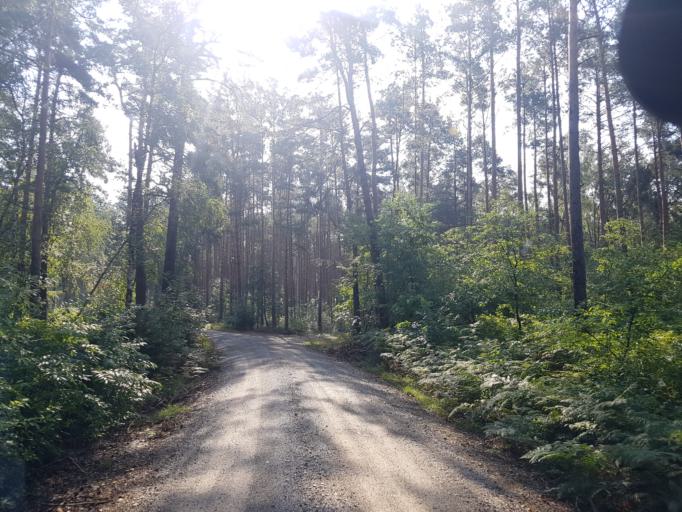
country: DE
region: Brandenburg
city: Hohenleipisch
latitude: 51.5143
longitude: 13.5853
